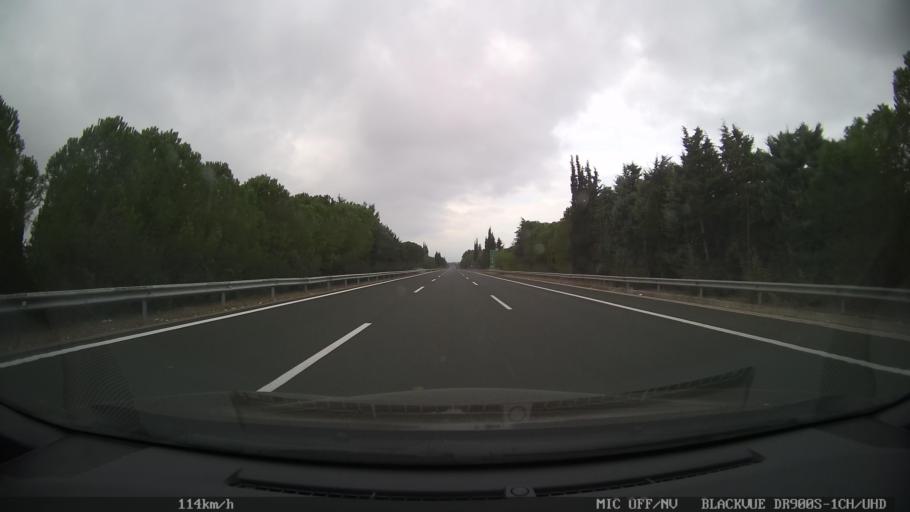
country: GR
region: Central Macedonia
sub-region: Nomos Pierias
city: Korinos
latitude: 40.3434
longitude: 22.5907
